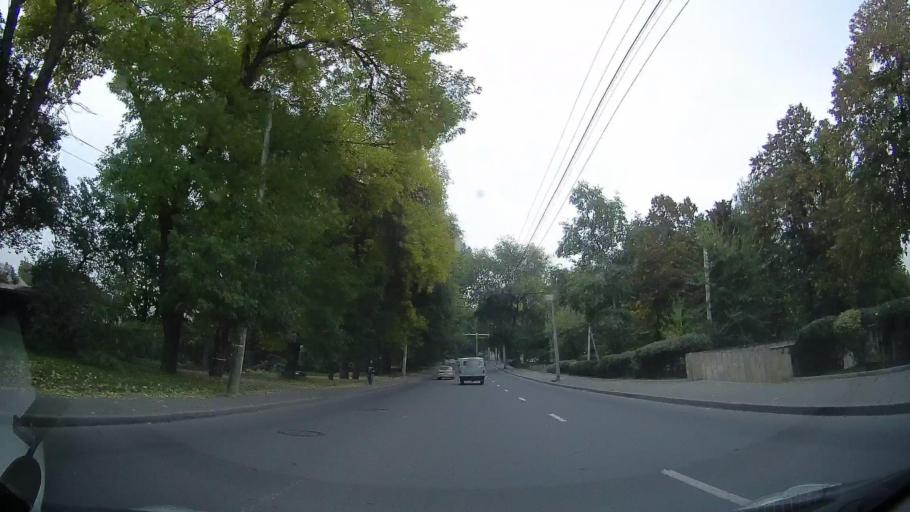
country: RU
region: Rostov
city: Severnyy
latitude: 47.2606
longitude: 39.6797
